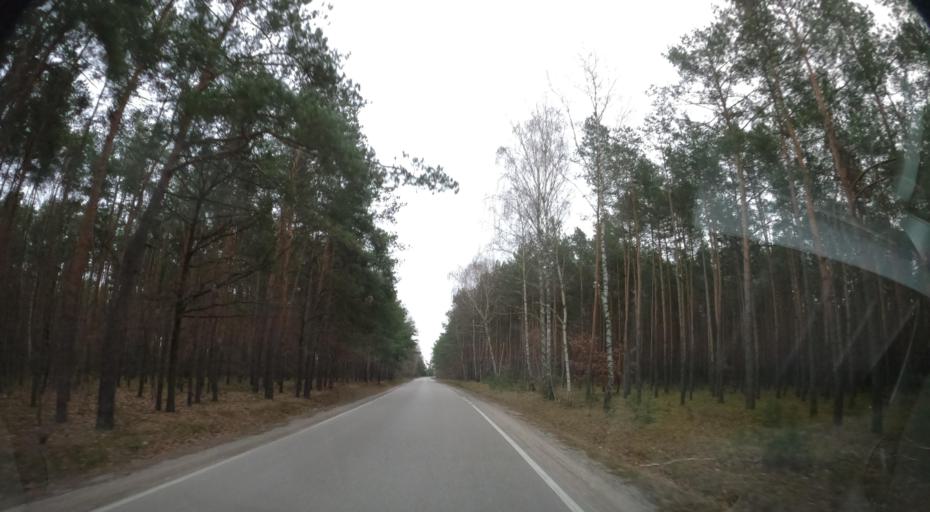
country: PL
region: Masovian Voivodeship
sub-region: Powiat radomski
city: Jedlinsk
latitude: 51.4896
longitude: 21.1688
